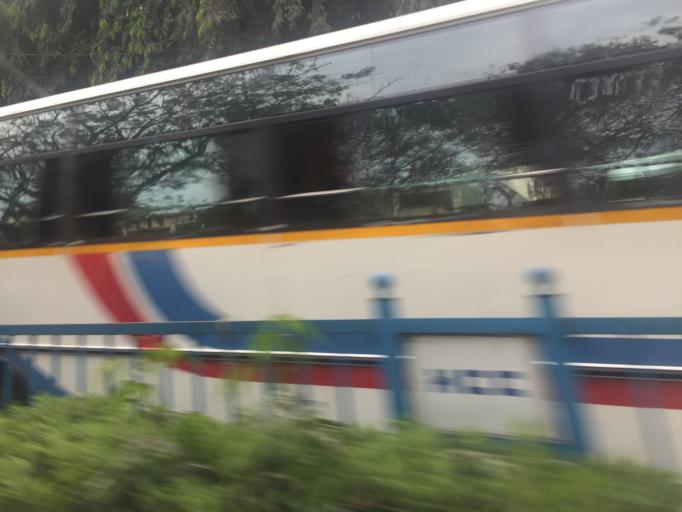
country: IN
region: Maharashtra
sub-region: Mumbai Suburban
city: Powai
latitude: 19.1195
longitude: 72.9259
